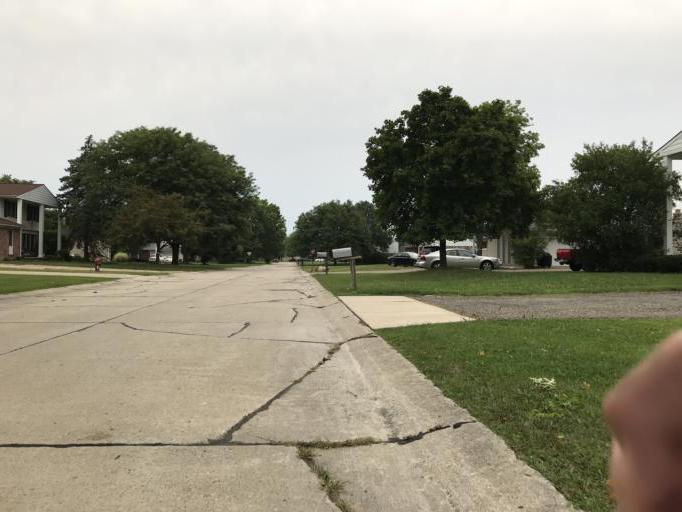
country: US
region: Michigan
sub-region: Oakland County
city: Franklin
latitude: 42.4869
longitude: -83.3198
